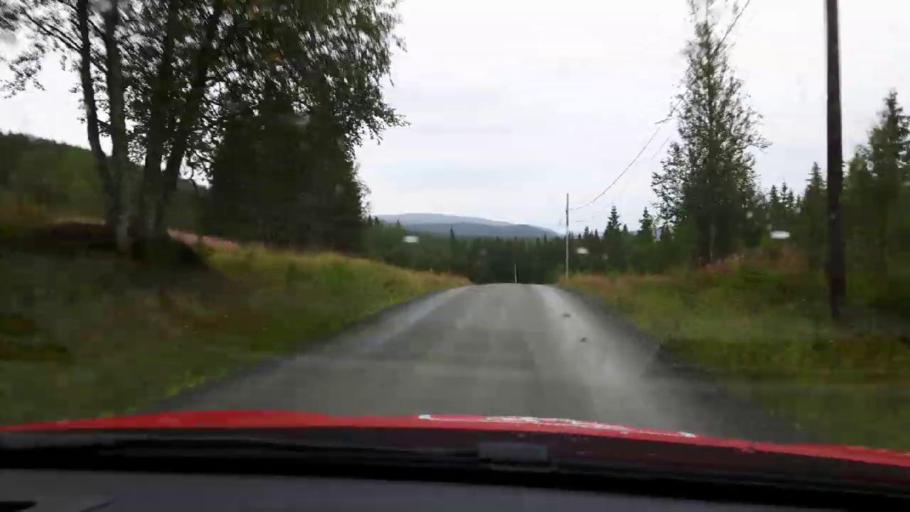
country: SE
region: Jaemtland
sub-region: Are Kommun
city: Are
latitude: 63.5022
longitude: 12.7520
